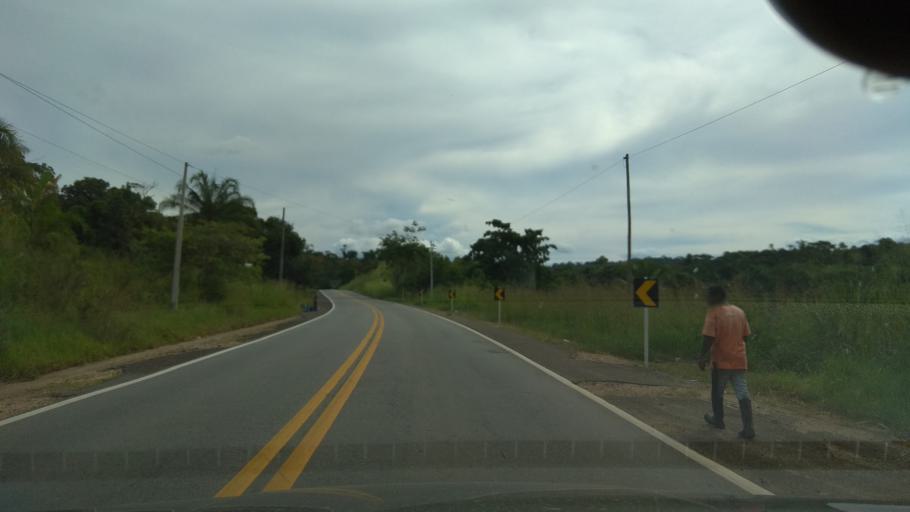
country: BR
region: Bahia
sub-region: Ubata
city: Ubata
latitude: -14.1938
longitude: -39.5507
